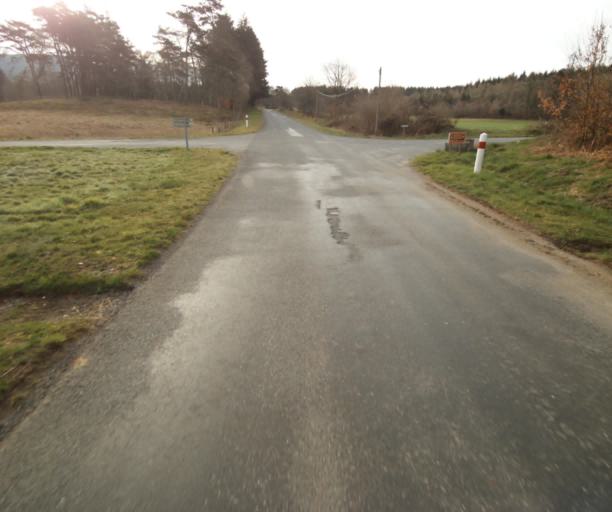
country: FR
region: Limousin
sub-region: Departement de la Correze
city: Treignac
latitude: 45.4723
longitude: 1.7977
